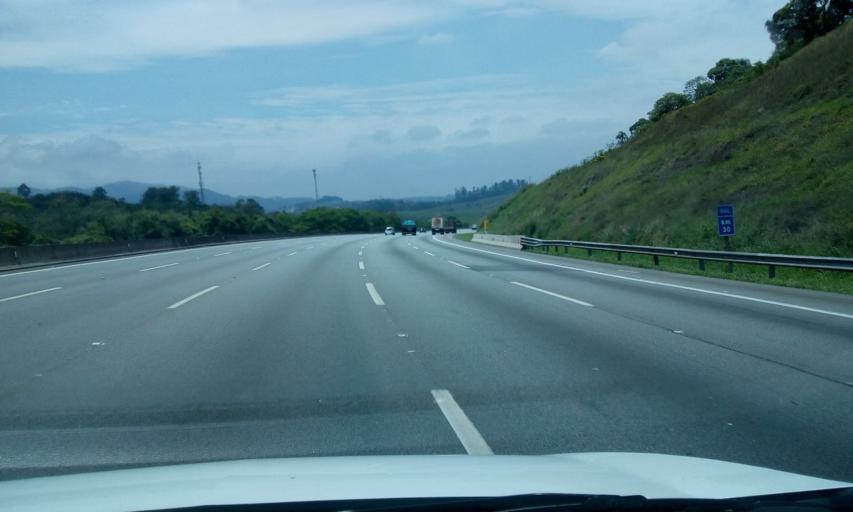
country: BR
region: Sao Paulo
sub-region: Caieiras
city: Caieiras
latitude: -23.3791
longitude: -46.7717
